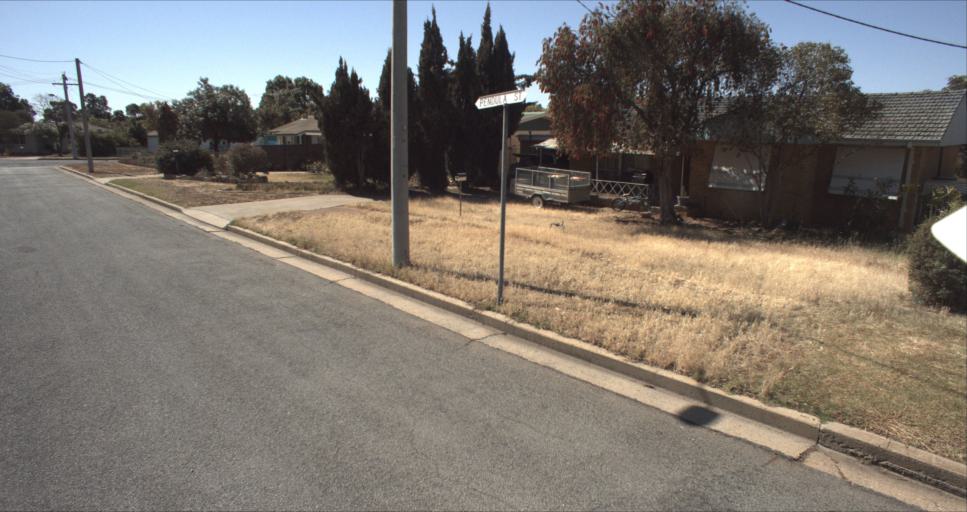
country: AU
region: New South Wales
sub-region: Leeton
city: Leeton
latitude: -34.5493
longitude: 146.3779
